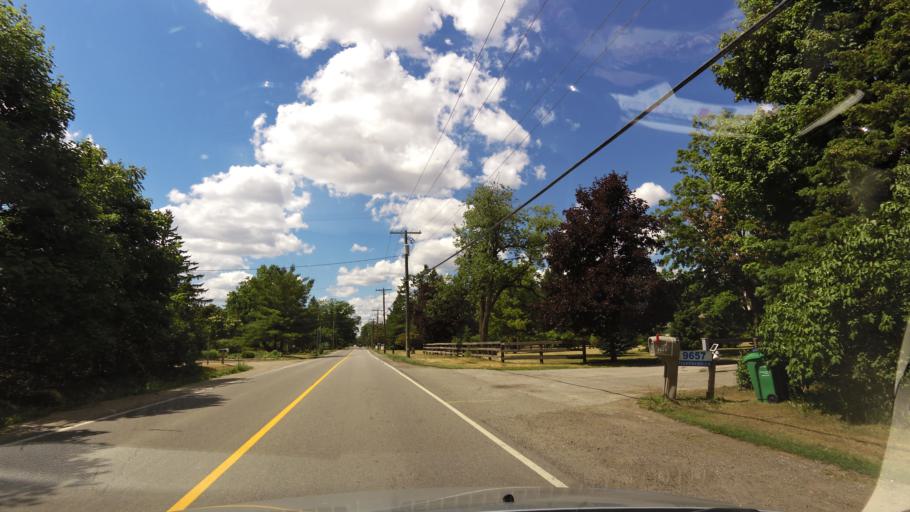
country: CA
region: Ontario
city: Brampton
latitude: 43.6402
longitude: -79.8420
